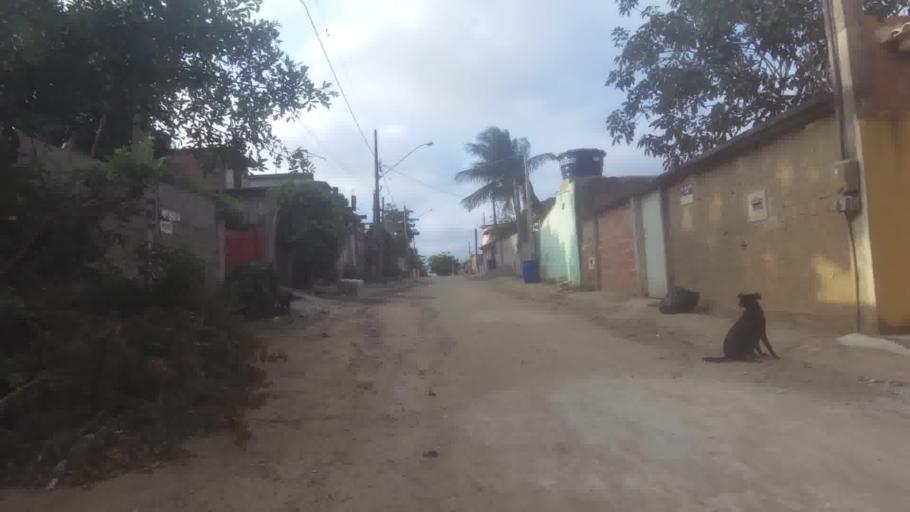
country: BR
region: Espirito Santo
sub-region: Itapemirim
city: Itapemirim
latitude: -21.0231
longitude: -40.8203
